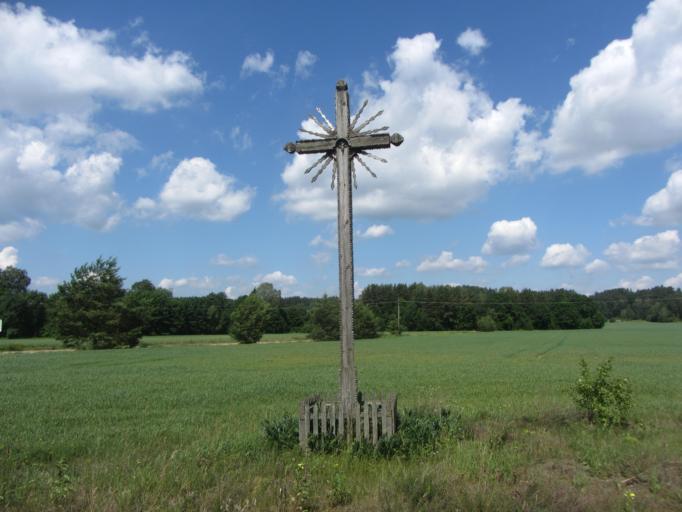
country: LT
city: Birstonas
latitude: 54.5547
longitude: 24.0263
